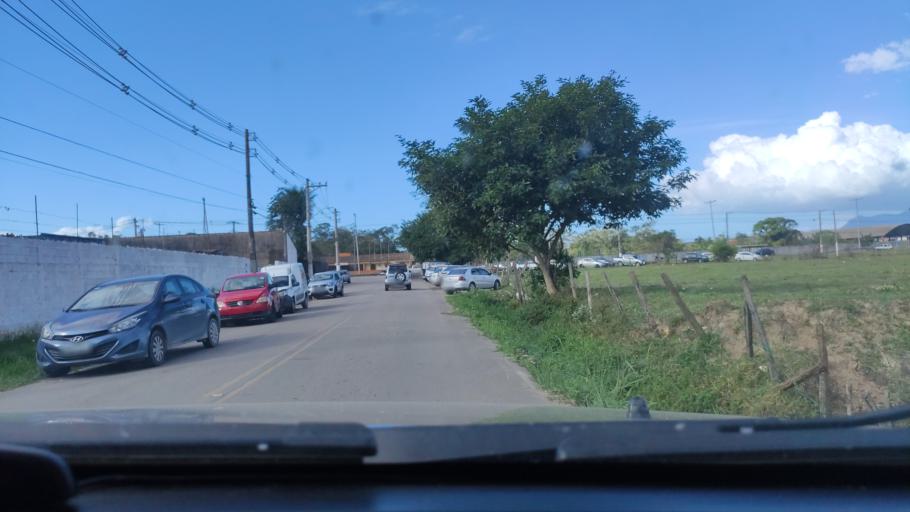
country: BR
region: Sao Paulo
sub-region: Sao Sebastiao
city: Sao Sebastiao
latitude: -23.6922
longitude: -45.4445
